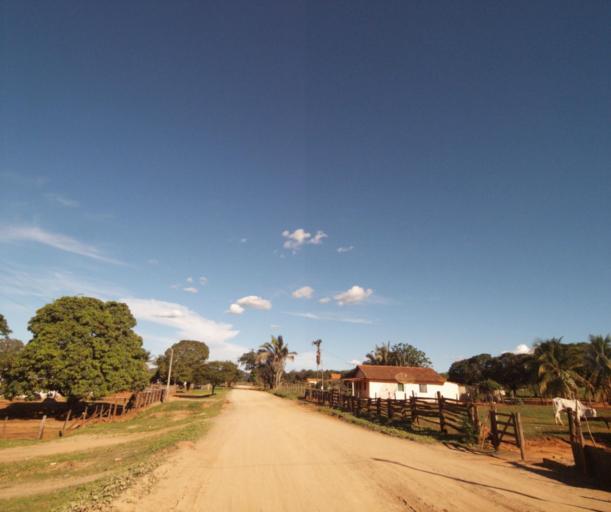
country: BR
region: Bahia
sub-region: Carinhanha
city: Carinhanha
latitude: -14.2786
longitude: -44.4981
